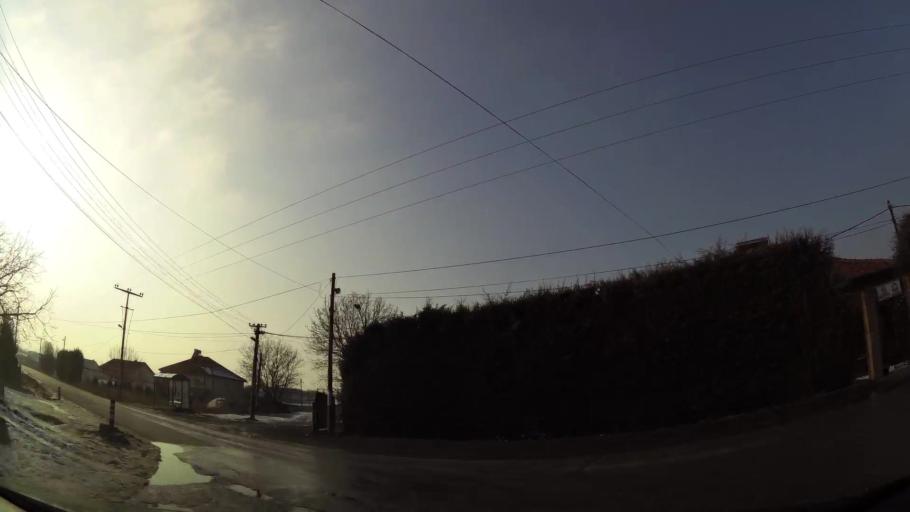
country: MK
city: Miladinovci
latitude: 41.9802
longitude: 21.6475
